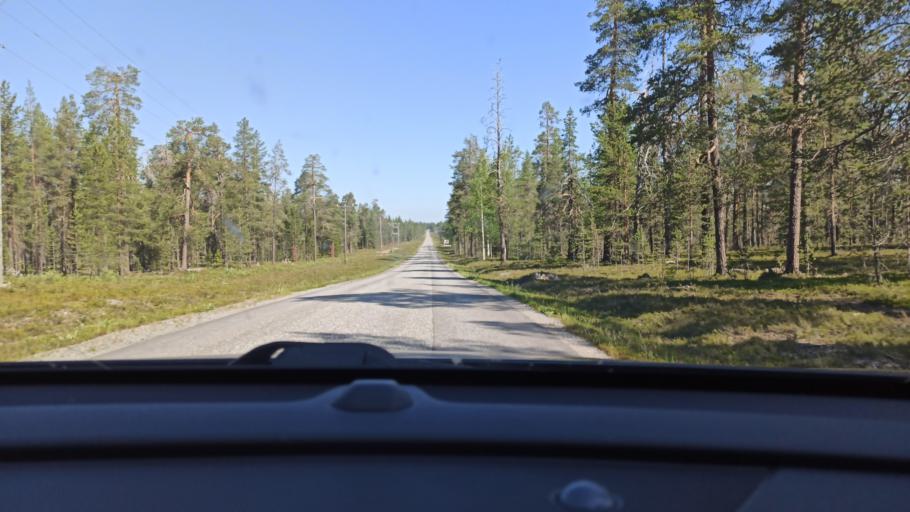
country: FI
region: Lapland
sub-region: Tunturi-Lappi
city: Kolari
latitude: 67.6430
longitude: 24.1588
